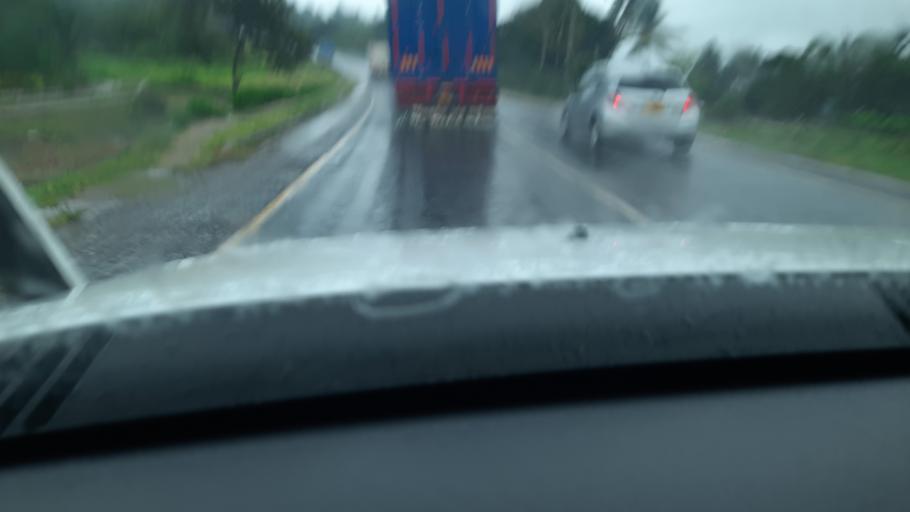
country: TZ
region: Pwani
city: Bagamoyo
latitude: -6.5869
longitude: 39.0531
